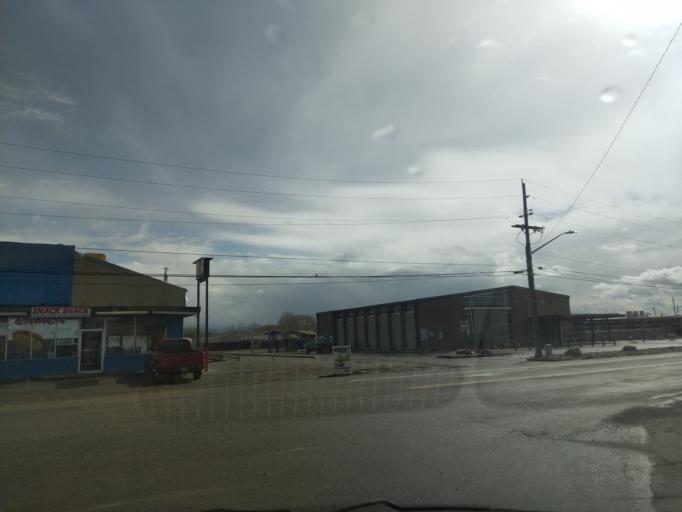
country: US
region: Colorado
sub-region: Mesa County
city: Grand Junction
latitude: 39.0755
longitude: -108.5338
